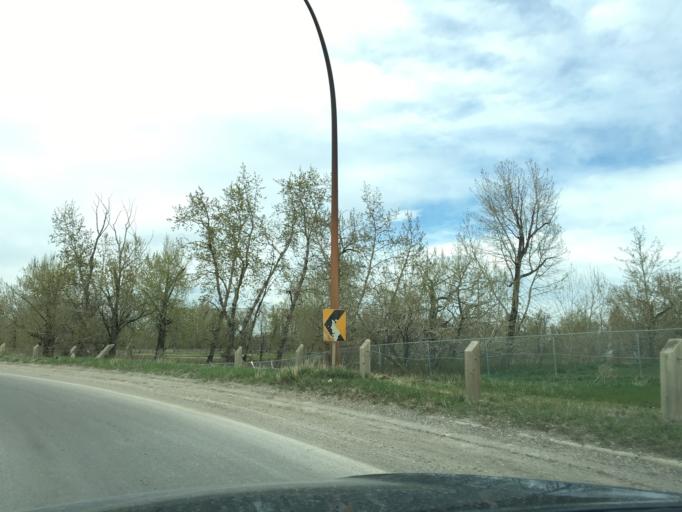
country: CA
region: Alberta
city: Calgary
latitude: 50.9680
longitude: -114.0291
